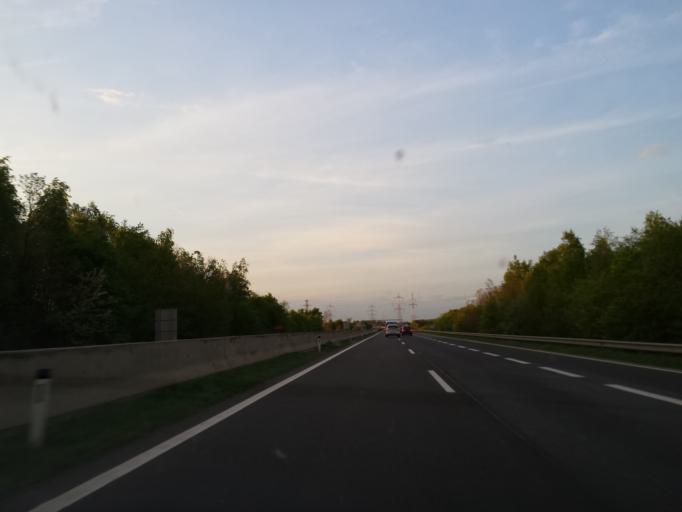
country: AT
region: Burgenland
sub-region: Politischer Bezirk Neusiedl am See
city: Parndorf
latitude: 48.0081
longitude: 16.8351
